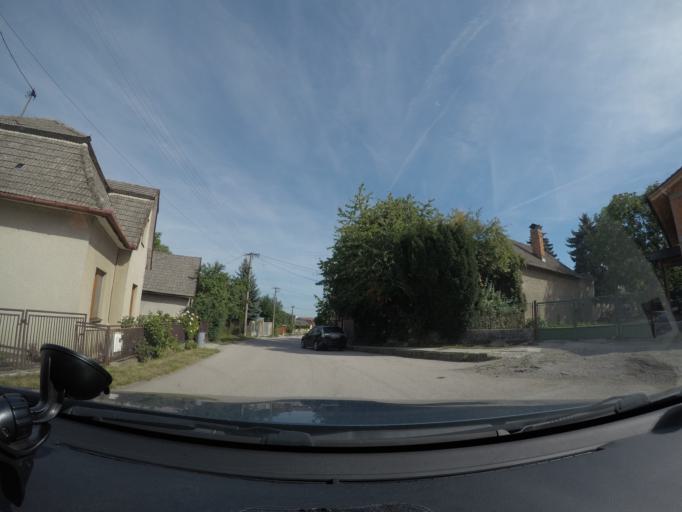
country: SK
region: Trenciansky
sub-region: Okres Trencin
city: Trencin
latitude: 48.7619
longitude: 18.1078
